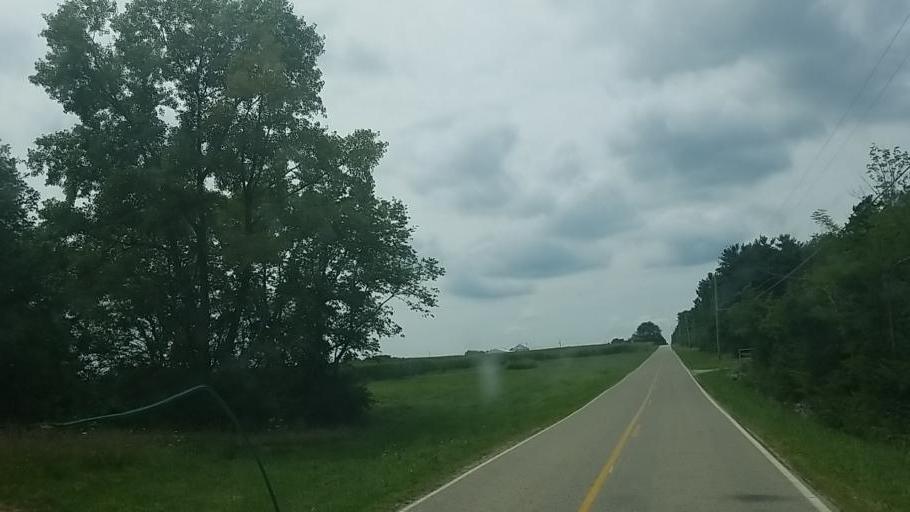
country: US
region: Ohio
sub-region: Fairfield County
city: Lithopolis
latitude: 39.7523
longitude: -82.8502
